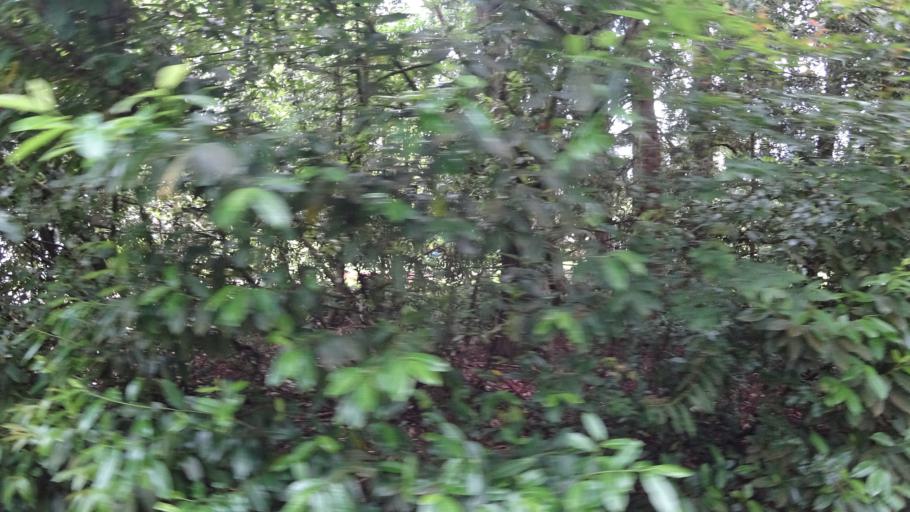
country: US
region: Oregon
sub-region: Washington County
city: Garden Home-Whitford
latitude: 45.4701
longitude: -122.7580
